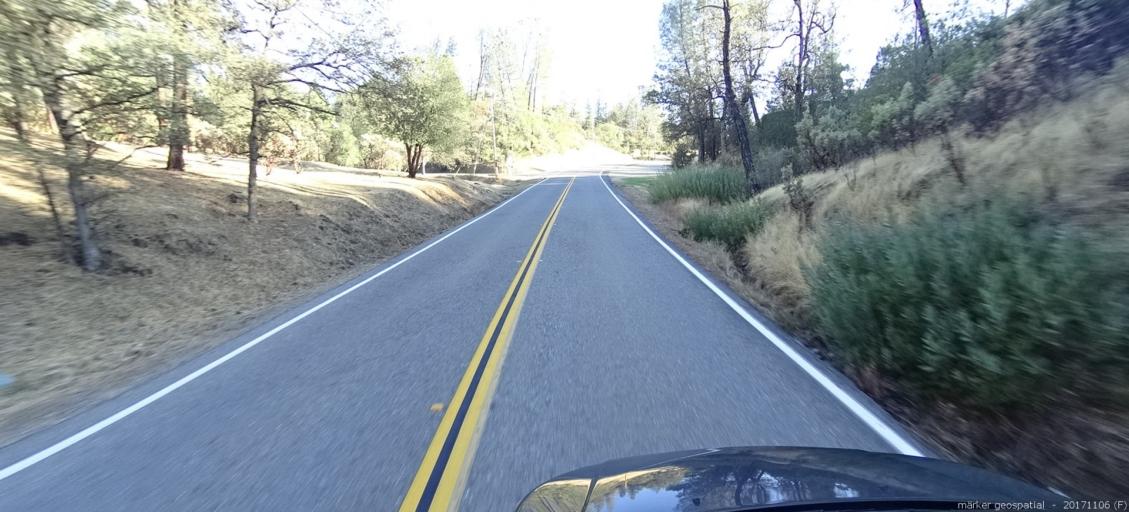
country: US
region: California
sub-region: Shasta County
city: Shasta
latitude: 40.5828
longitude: -122.4823
